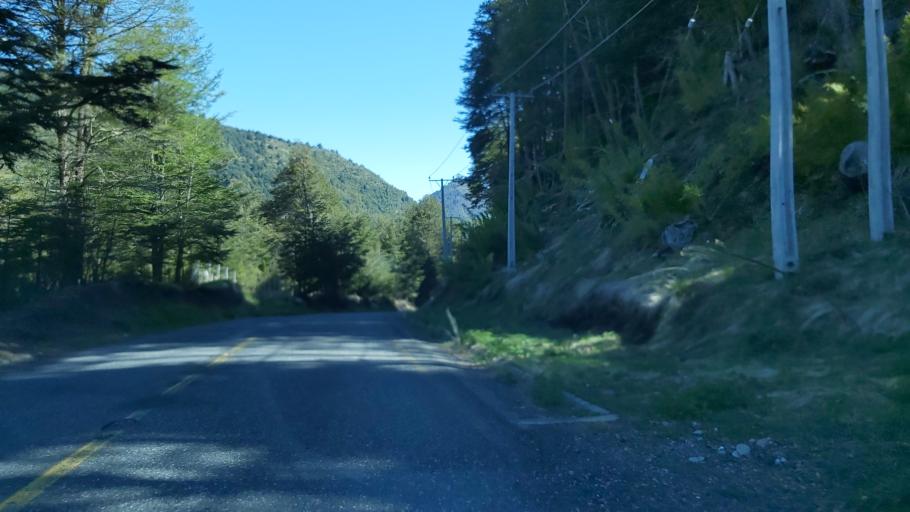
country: CL
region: Araucania
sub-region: Provincia de Cautin
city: Vilcun
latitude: -38.4609
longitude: -71.5164
